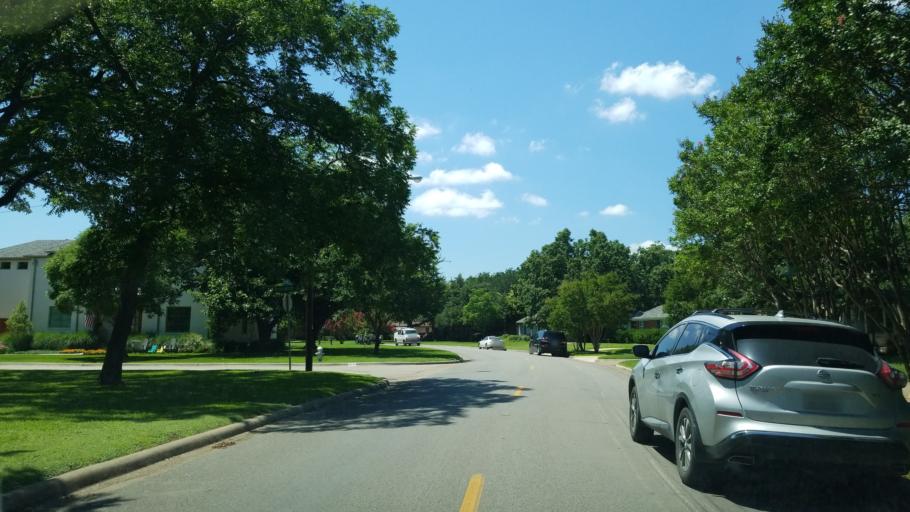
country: US
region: Texas
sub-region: Dallas County
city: University Park
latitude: 32.8746
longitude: -96.8397
